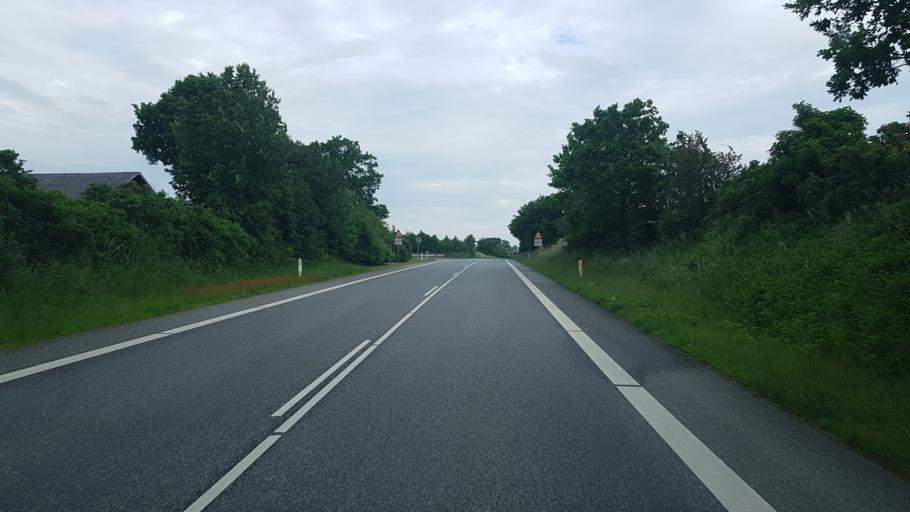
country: DK
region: South Denmark
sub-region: Vejen Kommune
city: Rodding
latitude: 55.3907
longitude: 9.0424
